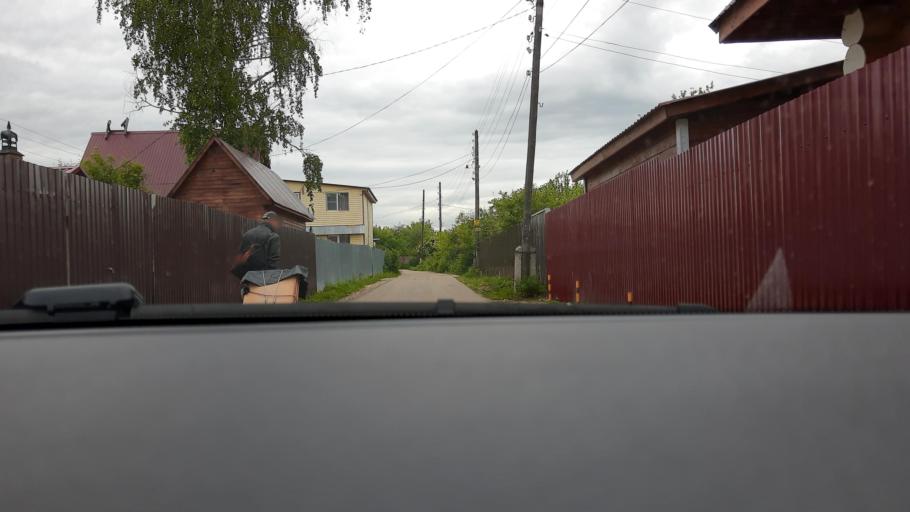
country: RU
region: Nizjnij Novgorod
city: Gorbatovka
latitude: 56.2598
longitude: 43.8294
